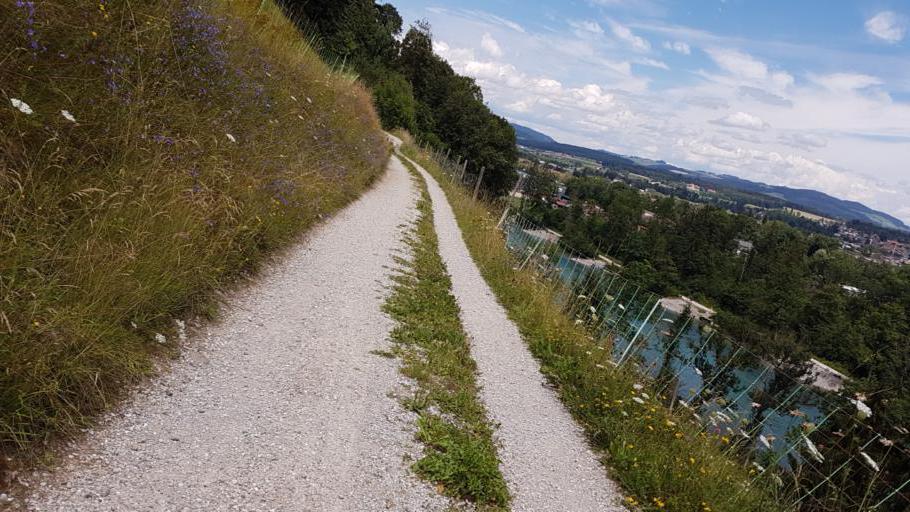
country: CH
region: Bern
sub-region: Bern-Mittelland District
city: Munsingen
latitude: 46.8603
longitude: 7.5491
